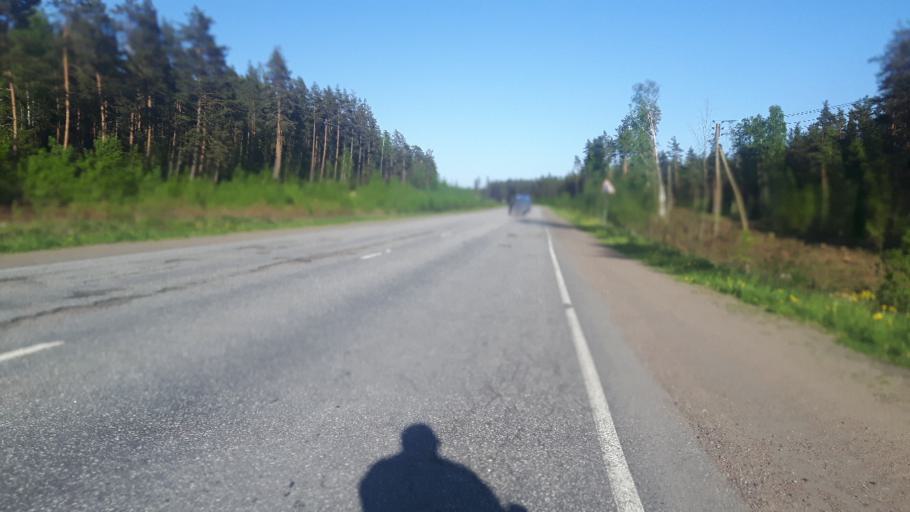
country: RU
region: Leningrad
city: Molodezhnoye
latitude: 60.1723
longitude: 29.2985
